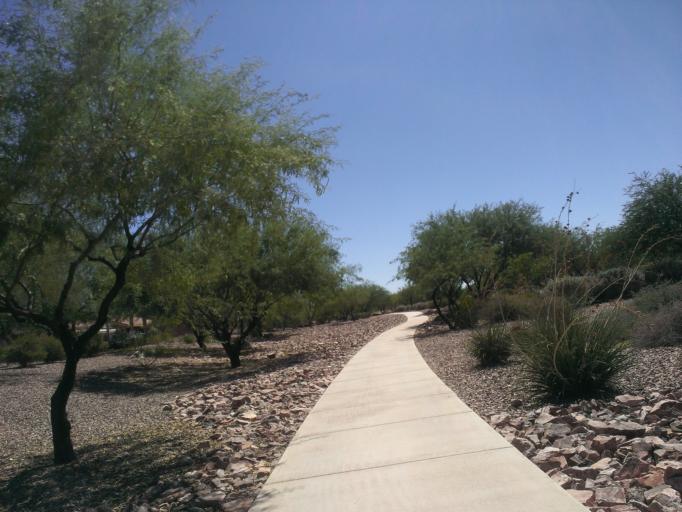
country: US
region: Arizona
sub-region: Pinal County
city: Arizona City
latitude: 32.8113
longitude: -111.6365
